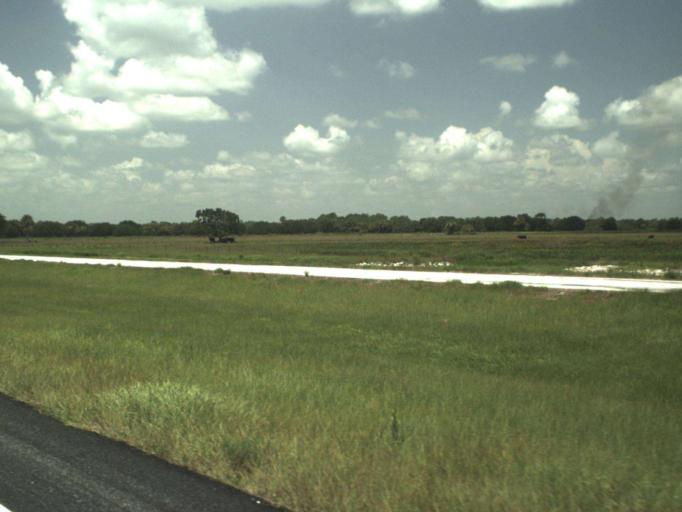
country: US
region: Florida
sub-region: Okeechobee County
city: Taylor Creek
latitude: 27.3459
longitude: -80.6398
